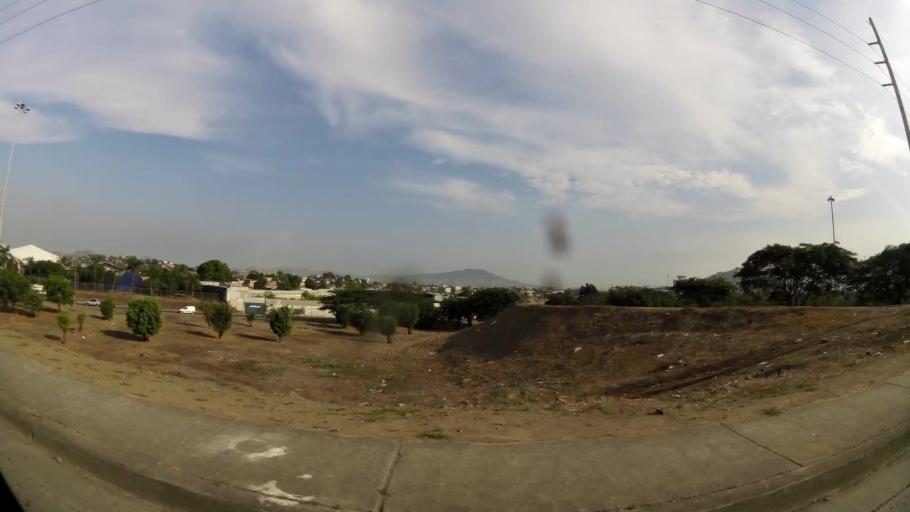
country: EC
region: Guayas
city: Eloy Alfaro
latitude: -2.0754
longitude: -79.9209
